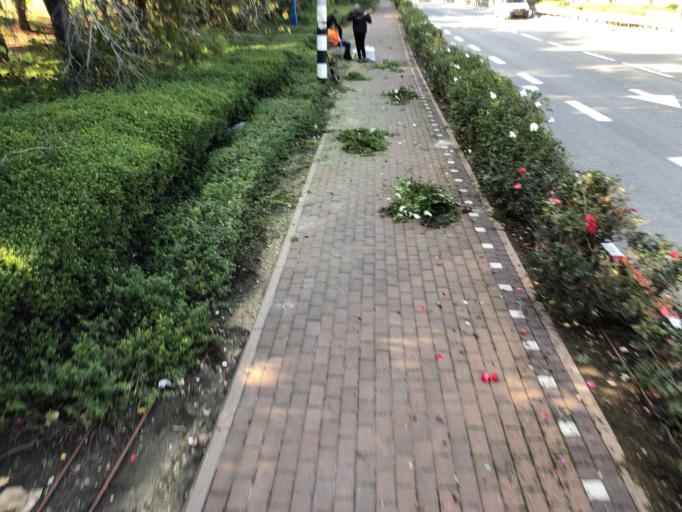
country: IL
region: Northern District
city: `Akko
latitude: 32.9219
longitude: 35.0909
